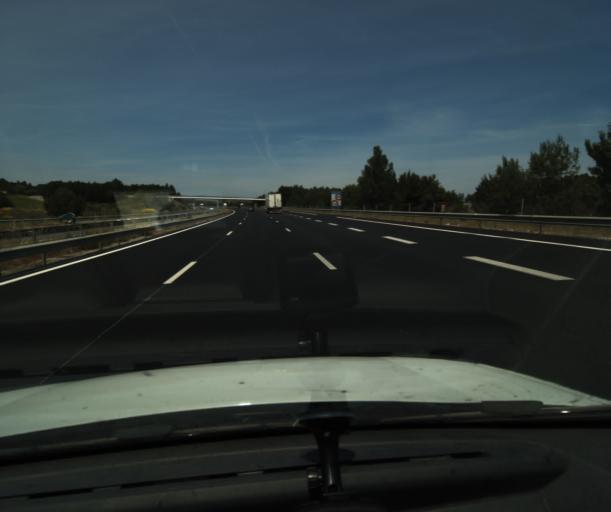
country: FR
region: Languedoc-Roussillon
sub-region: Departement de l'Aude
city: Sigean
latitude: 43.0351
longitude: 2.9527
